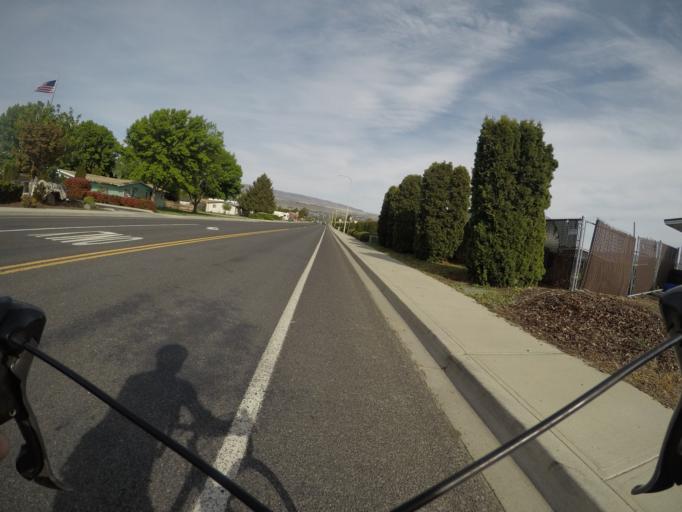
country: US
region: Washington
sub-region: Chelan County
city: West Wenatchee
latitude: 47.4425
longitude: -120.3459
